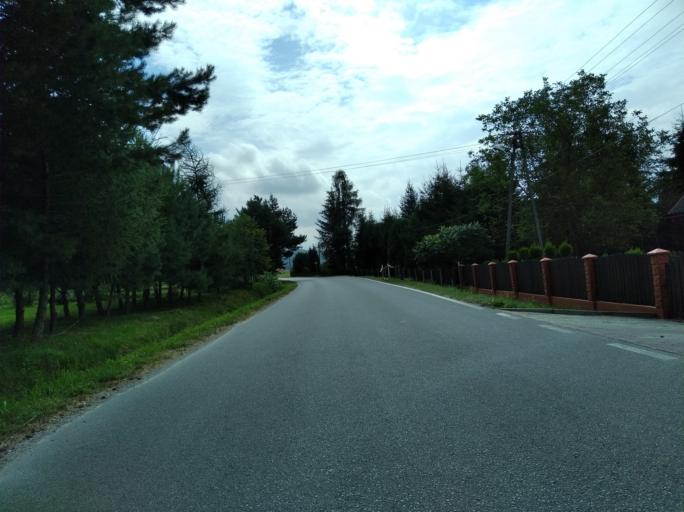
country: PL
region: Subcarpathian Voivodeship
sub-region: Powiat krosnienski
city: Leki
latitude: 49.7986
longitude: 21.6770
